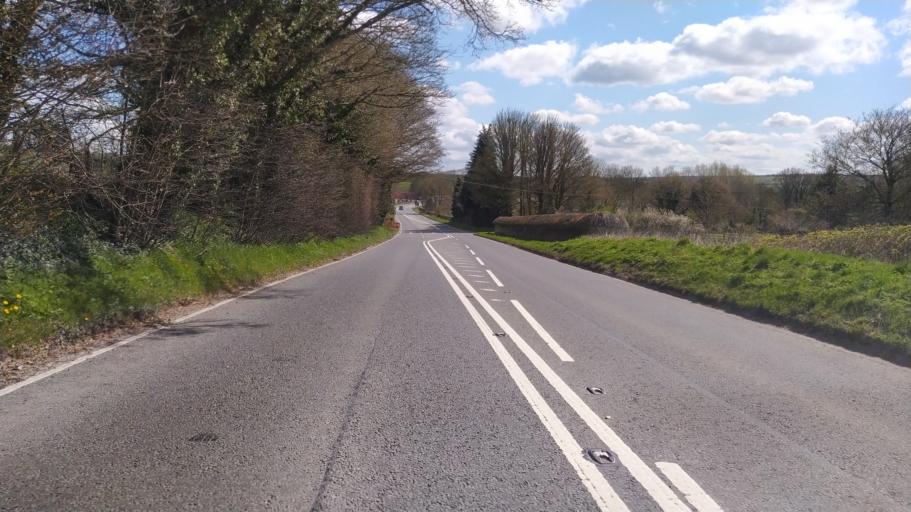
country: GB
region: England
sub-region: Wiltshire
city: Avebury
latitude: 51.4143
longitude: -1.8443
